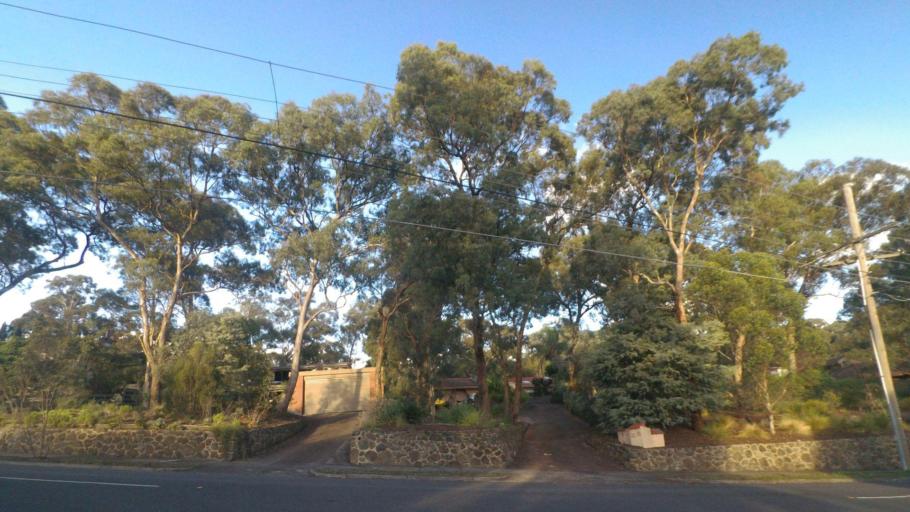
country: AU
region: Victoria
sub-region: Banyule
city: Lower Plenty
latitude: -37.7277
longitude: 145.1208
